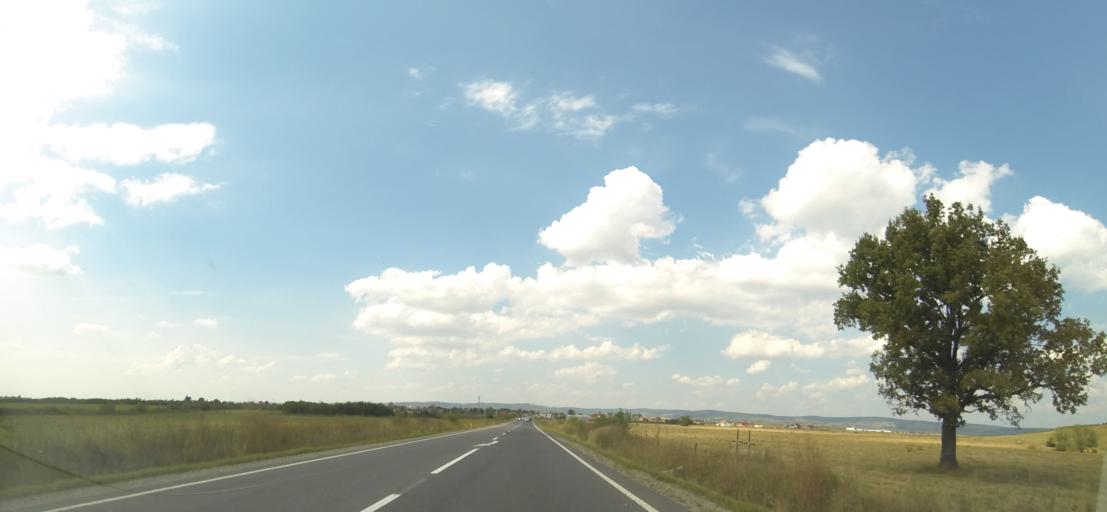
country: RO
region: Brasov
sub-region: Comuna Sercaia
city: Sercaia
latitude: 45.8243
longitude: 25.1559
